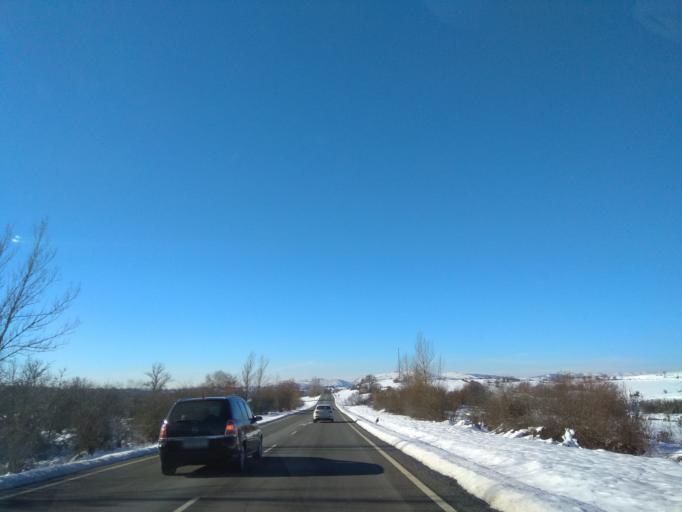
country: ES
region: Cantabria
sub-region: Provincia de Cantabria
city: San Martin de Elines
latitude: 42.9371
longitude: -3.7058
